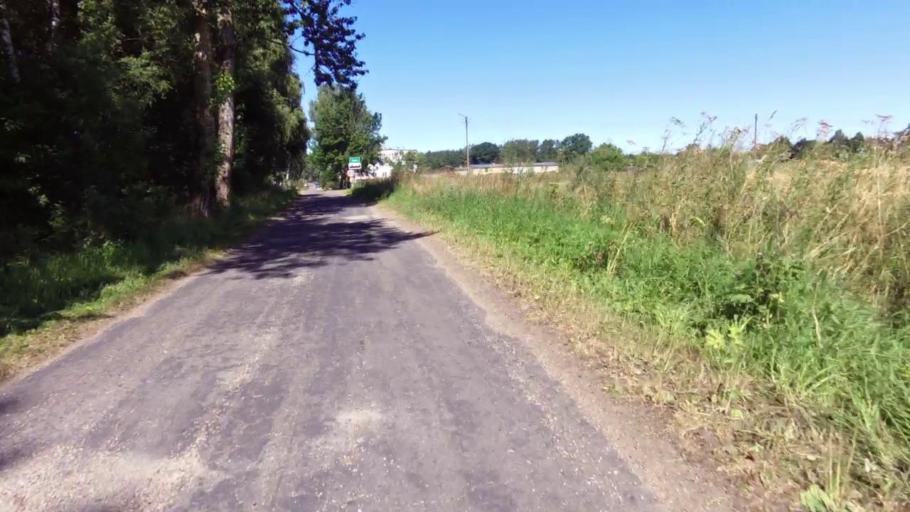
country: PL
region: West Pomeranian Voivodeship
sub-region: Powiat drawski
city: Czaplinek
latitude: 53.5356
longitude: 16.2128
